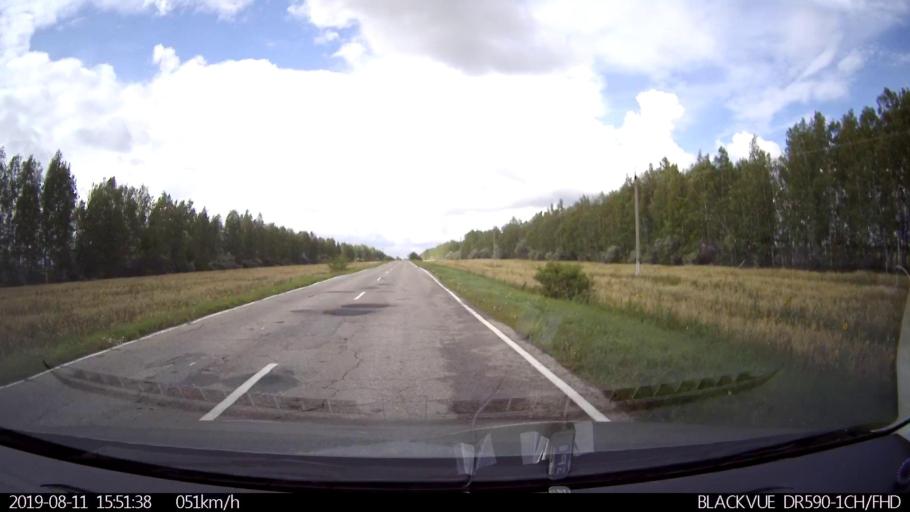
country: RU
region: Ulyanovsk
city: Ignatovka
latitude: 53.9202
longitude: 47.6561
